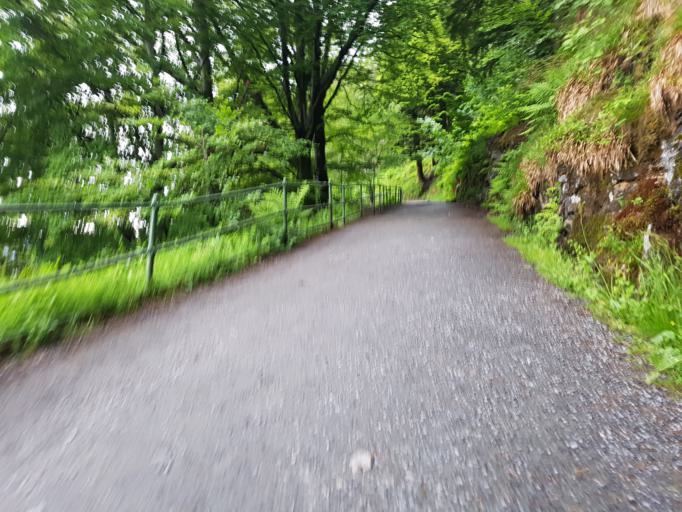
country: NO
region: Hordaland
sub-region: Bergen
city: Bergen
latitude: 60.3961
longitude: 5.3393
